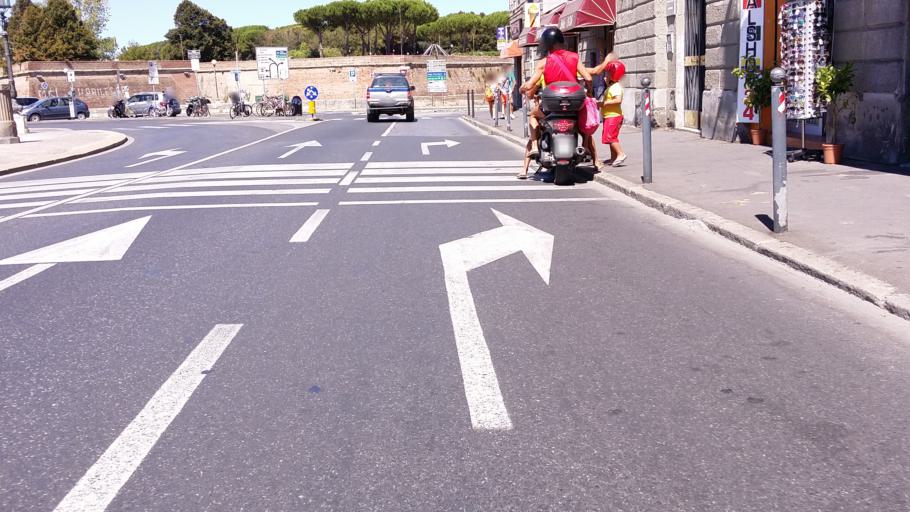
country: IT
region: Tuscany
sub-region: Provincia di Livorno
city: Livorno
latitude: 43.5531
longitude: 10.3140
